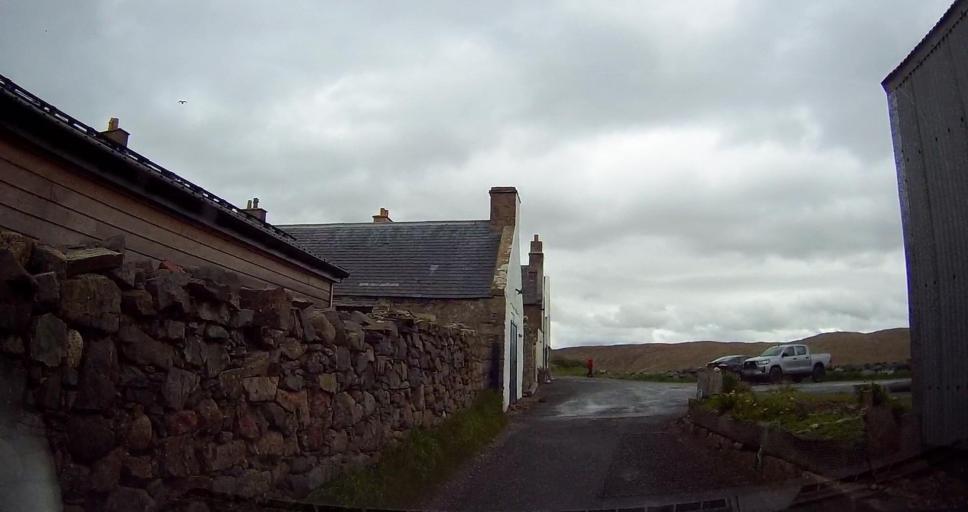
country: GB
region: Scotland
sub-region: Shetland Islands
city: Lerwick
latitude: 60.4758
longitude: -1.4891
